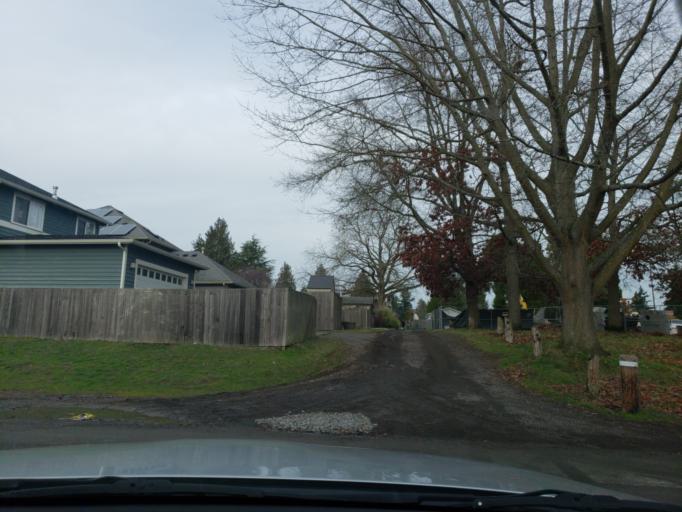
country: US
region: Washington
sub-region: King County
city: Shoreline
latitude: 47.7069
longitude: -122.3508
